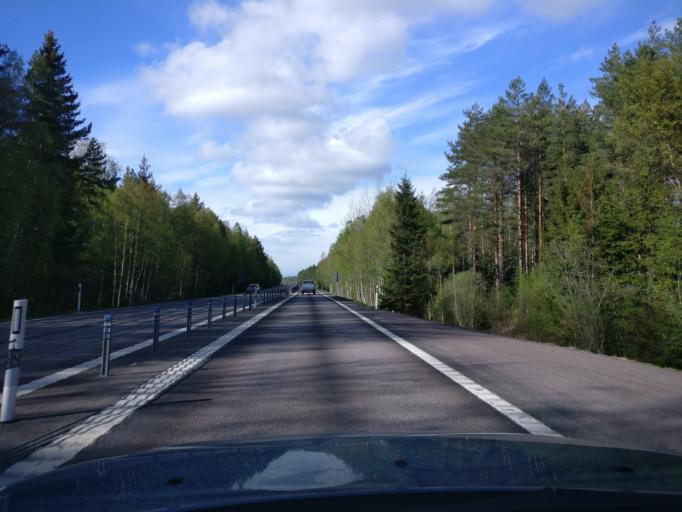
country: SE
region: Vaermland
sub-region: Forshaga Kommun
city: Forshaga
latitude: 59.4481
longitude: 13.4169
